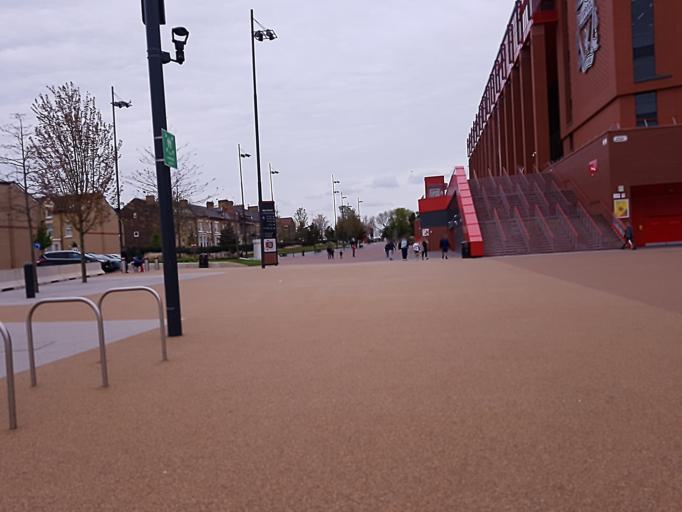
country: GB
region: England
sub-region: Liverpool
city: Liverpool
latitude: 53.4308
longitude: -2.9634
